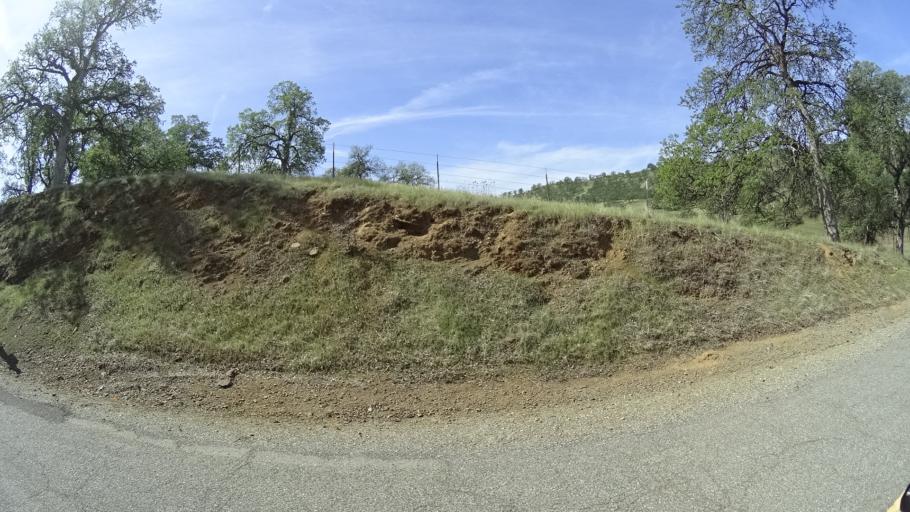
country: US
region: California
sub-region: Glenn County
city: Willows
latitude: 39.5434
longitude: -122.4279
